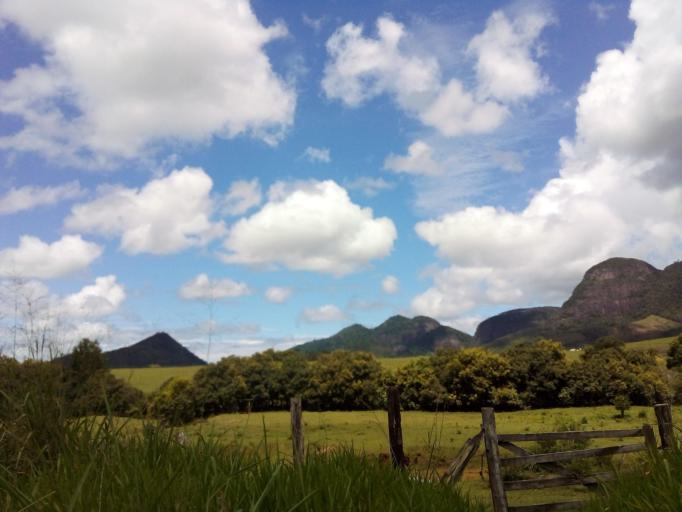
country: BR
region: Espirito Santo
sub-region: Ibiracu
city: Ibiracu
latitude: -19.8811
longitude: -40.3630
